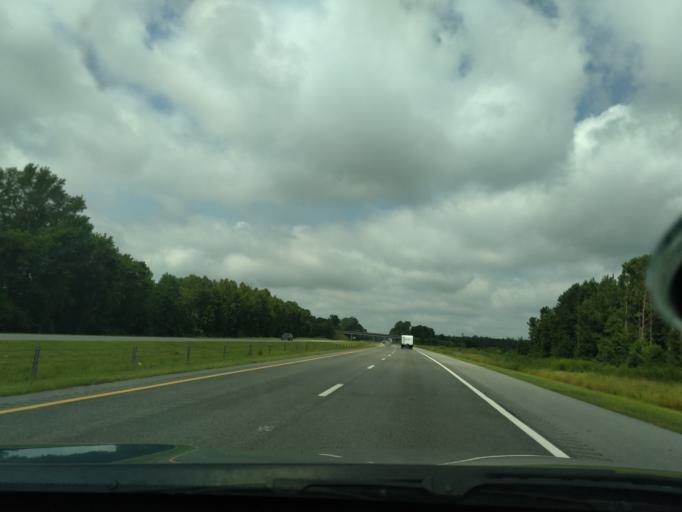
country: US
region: North Carolina
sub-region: Martin County
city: Robersonville
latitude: 35.8337
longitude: -77.3134
